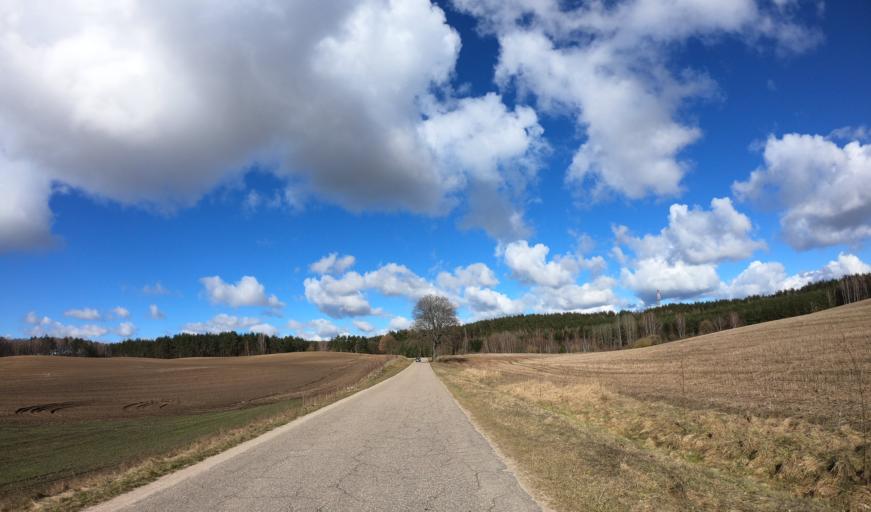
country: PL
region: West Pomeranian Voivodeship
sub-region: Powiat drawski
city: Zlocieniec
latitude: 53.4708
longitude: 15.9288
